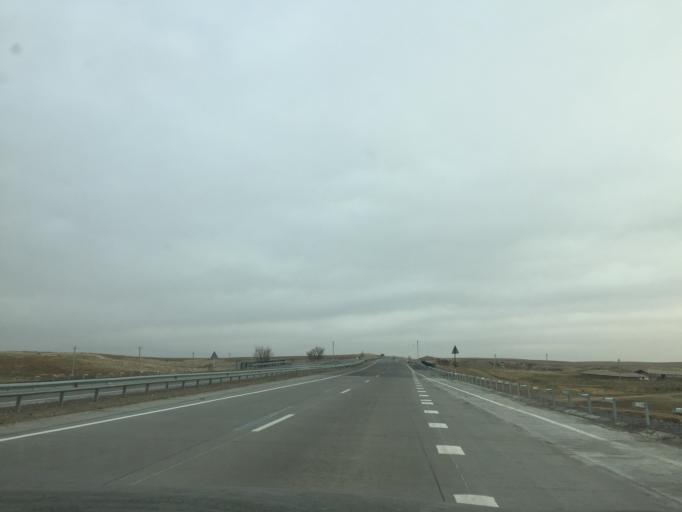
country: KZ
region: Ongtustik Qazaqstan
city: Aksu
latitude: 42.4421
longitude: 69.7271
